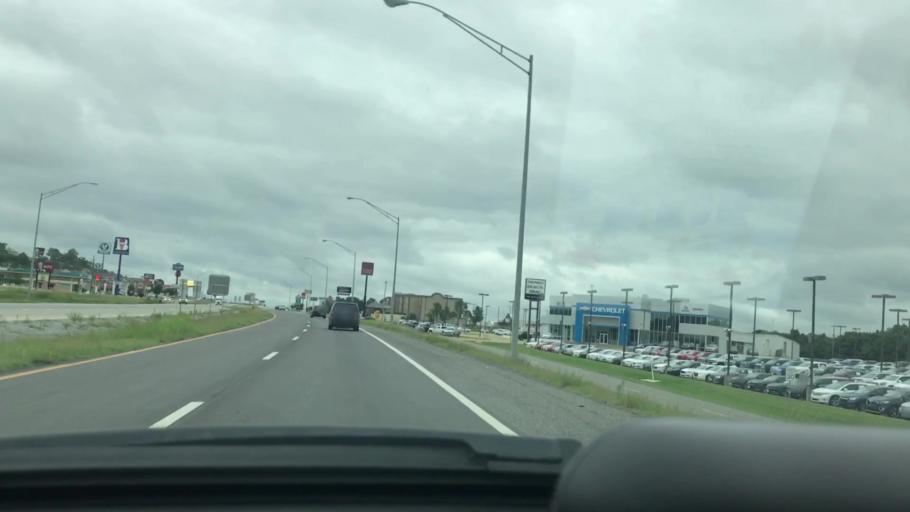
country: US
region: Oklahoma
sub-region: Pittsburg County
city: McAlester
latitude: 34.9103
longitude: -95.7452
